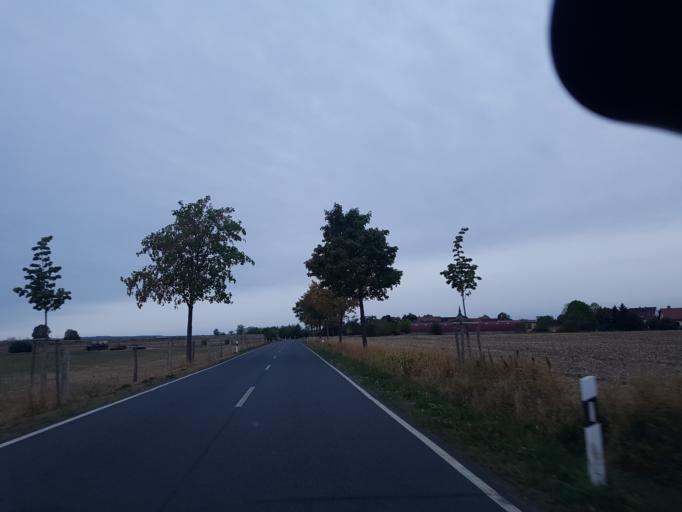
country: DE
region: Brandenburg
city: Muhlberg
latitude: 51.4929
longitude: 13.1914
